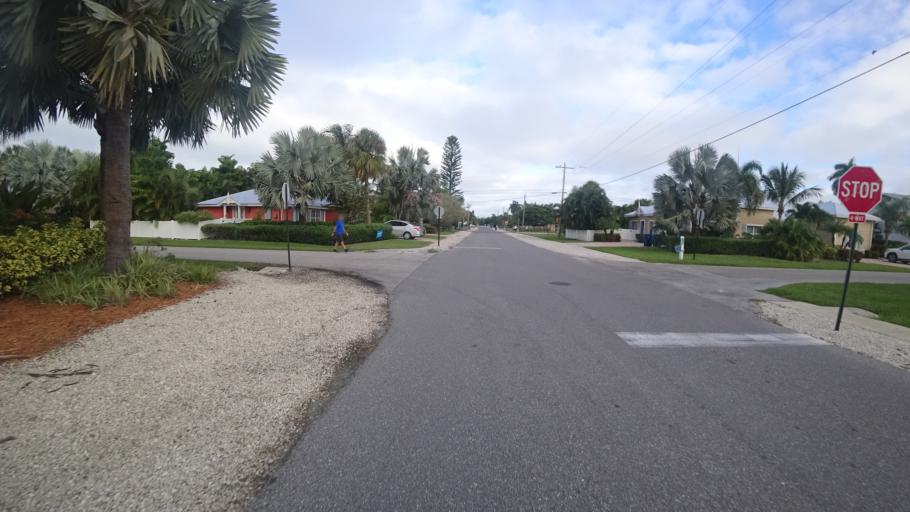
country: US
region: Florida
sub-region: Manatee County
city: Holmes Beach
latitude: 27.5136
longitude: -82.7204
